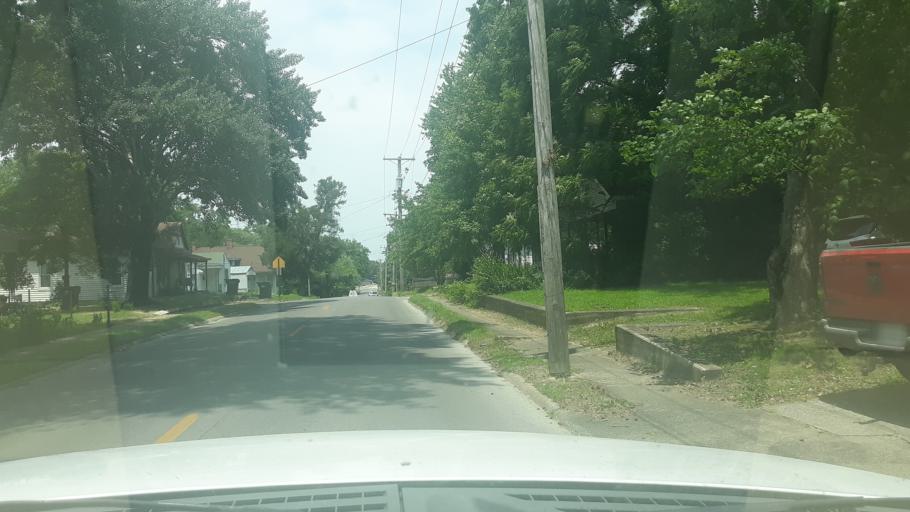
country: US
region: Illinois
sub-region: Saline County
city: Harrisburg
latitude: 37.7242
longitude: -88.5530
